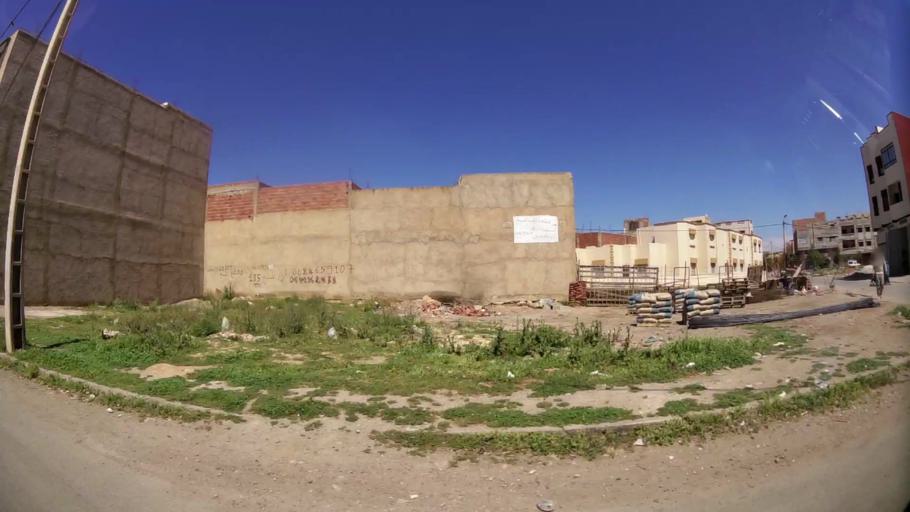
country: MA
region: Oriental
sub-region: Oujda-Angad
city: Oujda
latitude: 34.6896
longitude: -1.9354
